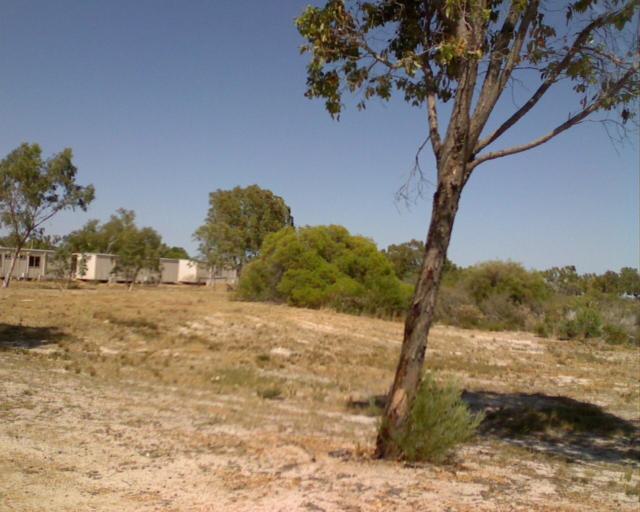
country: AU
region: Western Australia
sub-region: Dandaragan
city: Jurien Bay
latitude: -29.8172
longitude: 115.2676
